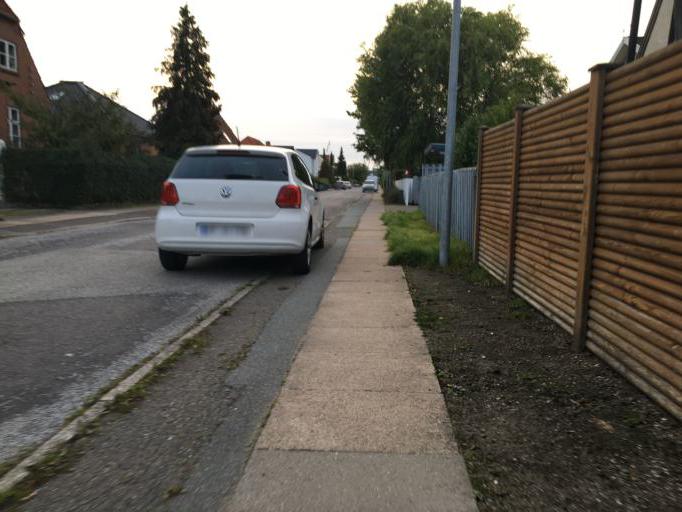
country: DK
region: Capital Region
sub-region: Tarnby Kommune
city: Tarnby
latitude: 55.6389
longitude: 12.6273
